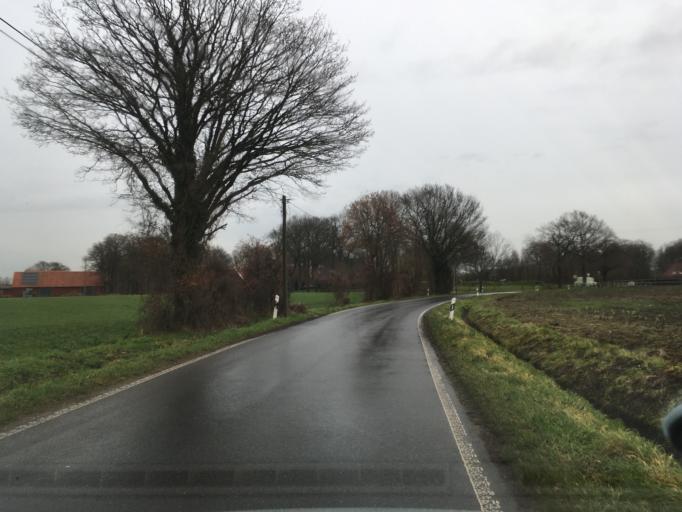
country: DE
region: North Rhine-Westphalia
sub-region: Regierungsbezirk Munster
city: Heek
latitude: 52.1378
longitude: 7.1166
